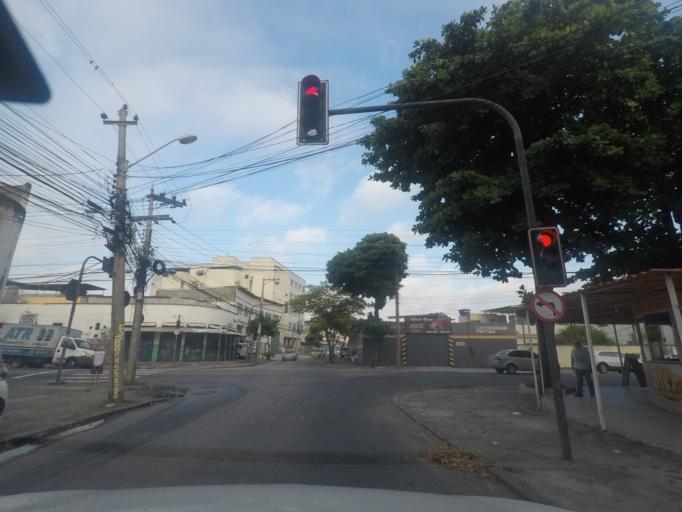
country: BR
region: Rio de Janeiro
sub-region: Duque De Caxias
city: Duque de Caxias
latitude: -22.8330
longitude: -43.2764
